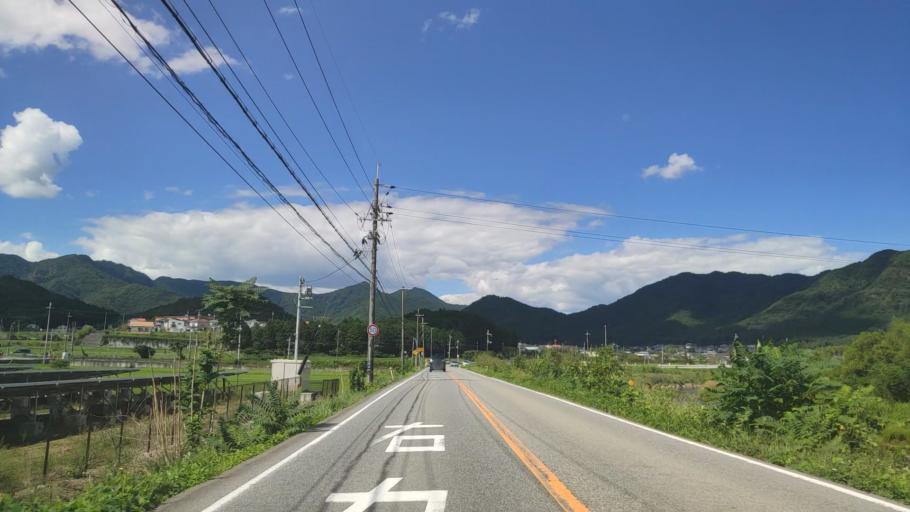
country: JP
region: Kyoto
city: Fukuchiyama
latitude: 35.1903
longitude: 135.1203
